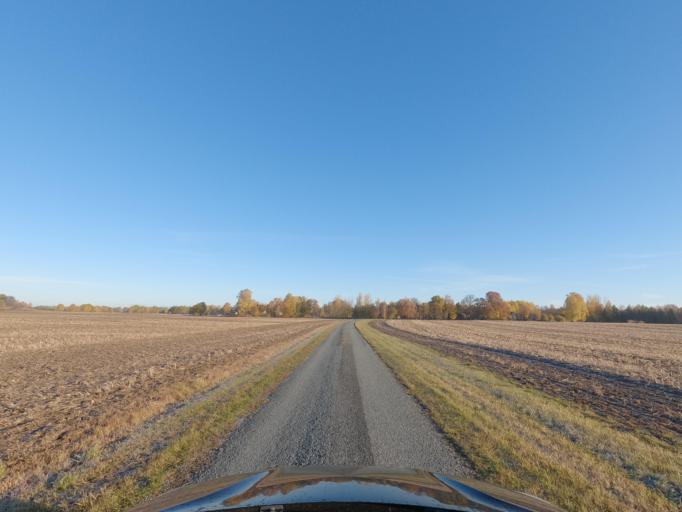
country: EE
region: Raplamaa
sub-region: Rapla vald
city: Rapla
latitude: 59.0544
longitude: 24.8579
